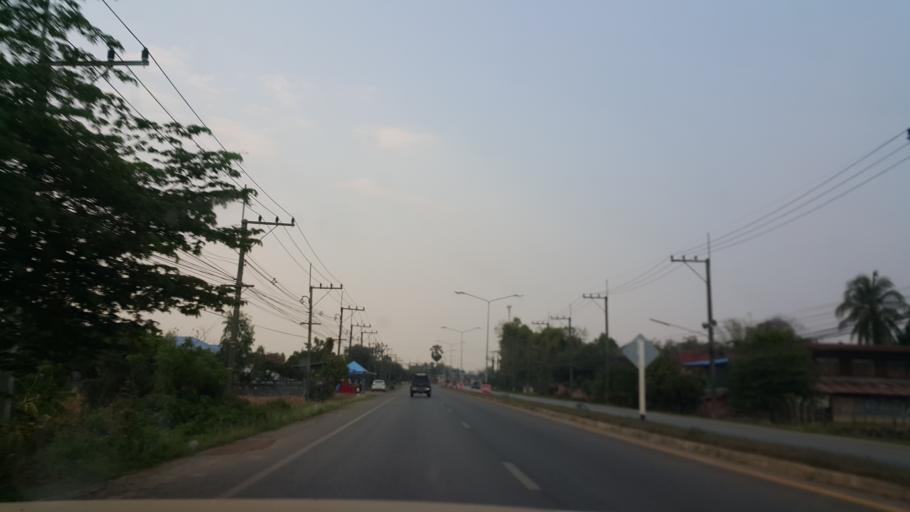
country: TH
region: Nakhon Phanom
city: Renu Nakhon
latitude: 17.0059
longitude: 104.7230
